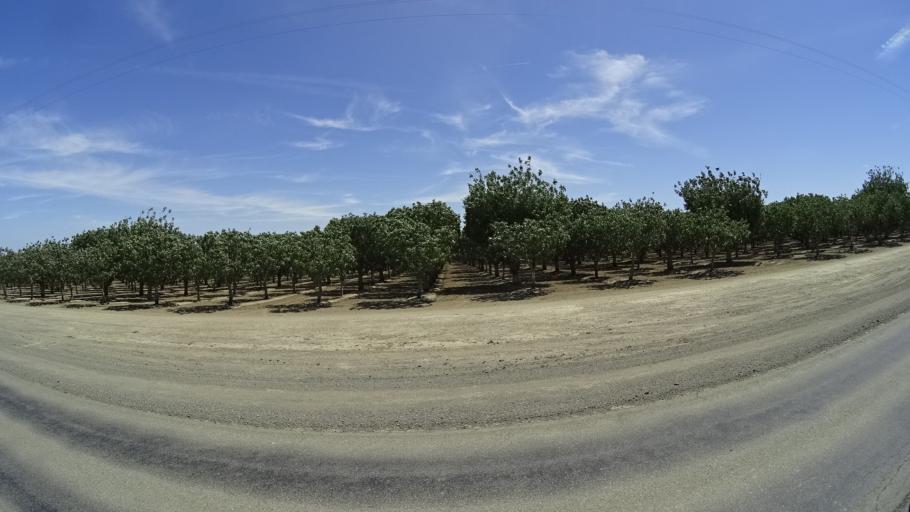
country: US
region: California
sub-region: Kings County
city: Kettleman City
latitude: 35.9139
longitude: -119.9150
